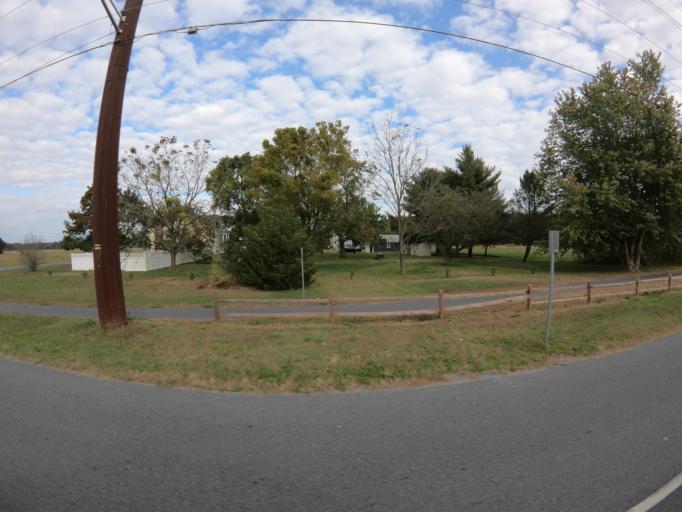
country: US
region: Delaware
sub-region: Sussex County
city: Milton
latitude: 38.7324
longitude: -75.2480
